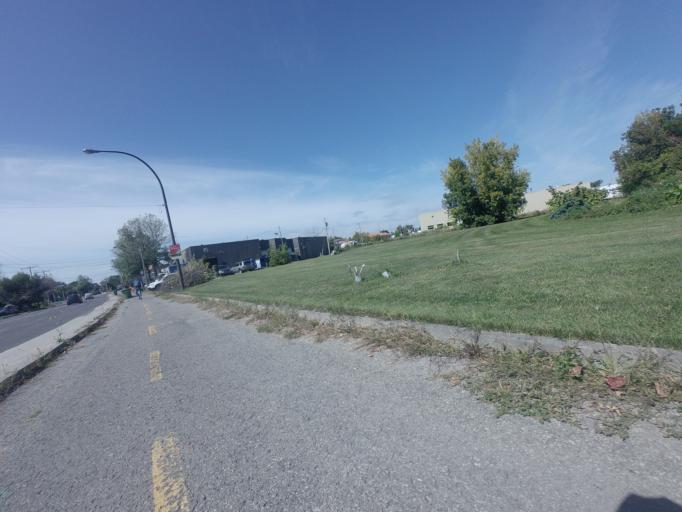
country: CA
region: Quebec
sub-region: Laurentides
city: Saint-Eustache
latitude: 45.5662
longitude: -73.9230
